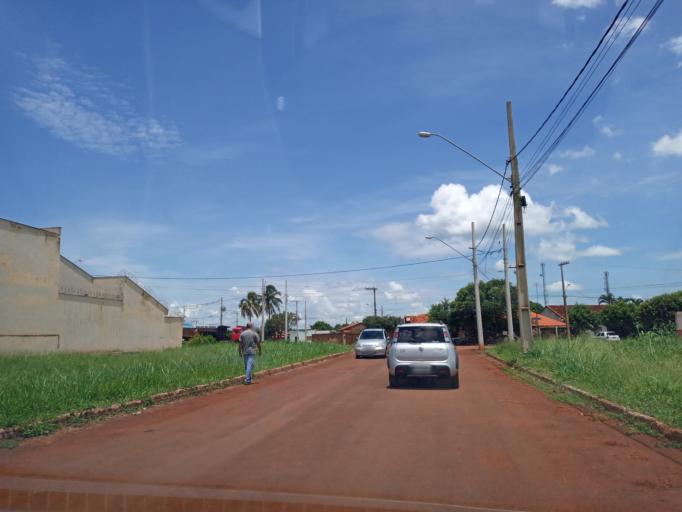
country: BR
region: Goias
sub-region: Itumbiara
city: Itumbiara
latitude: -18.4282
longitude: -49.1857
